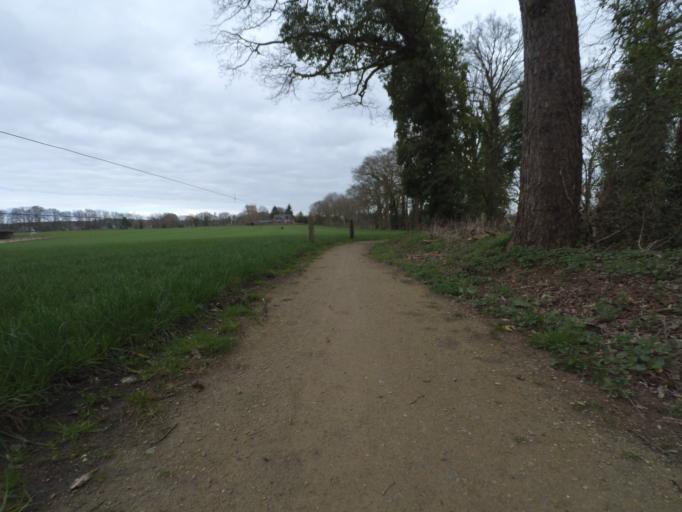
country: NL
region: Gelderland
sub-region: Gemeente Apeldoorn
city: Loenen
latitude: 52.1100
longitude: 6.0159
